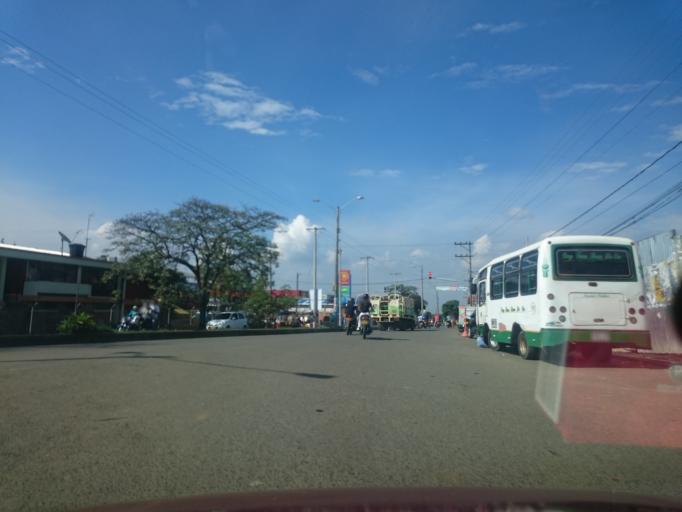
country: CO
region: Cauca
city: Santander de Quilichao
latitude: 3.0091
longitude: -76.4852
